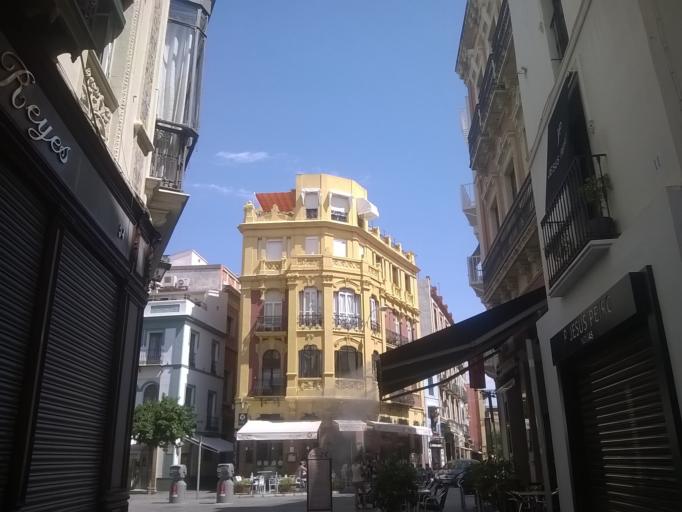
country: ES
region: Andalusia
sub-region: Provincia de Sevilla
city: Sevilla
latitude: 37.3890
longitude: -5.9933
